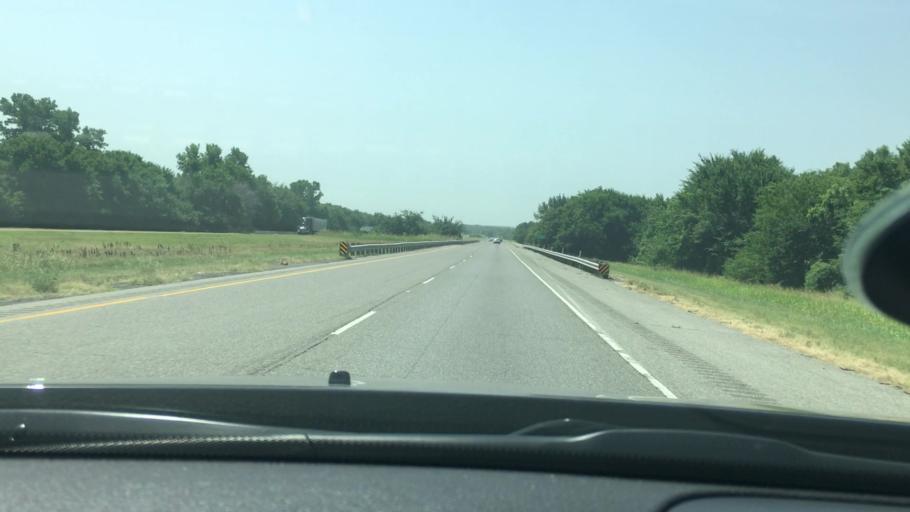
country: US
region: Oklahoma
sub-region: Murray County
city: Davis
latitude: 34.5354
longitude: -97.1882
